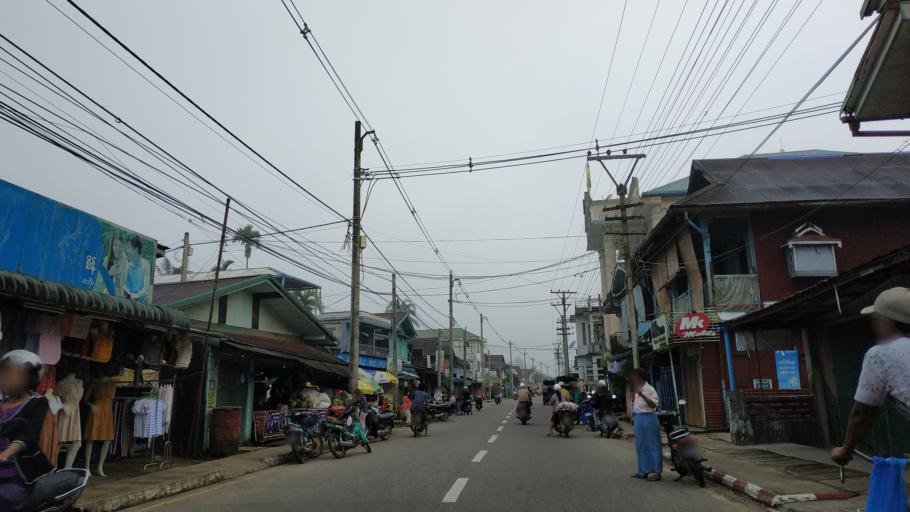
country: MM
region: Tanintharyi
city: Dawei
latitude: 14.0780
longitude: 98.1930
